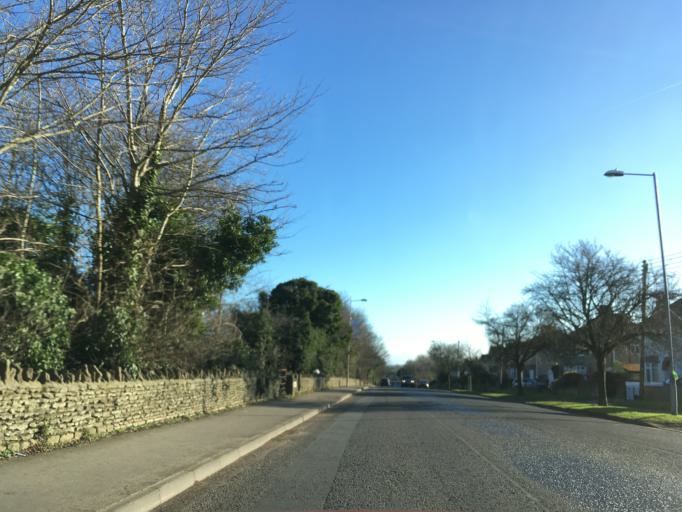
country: GB
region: England
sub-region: Wiltshire
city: Chippenham
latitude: 51.4651
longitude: -2.1330
